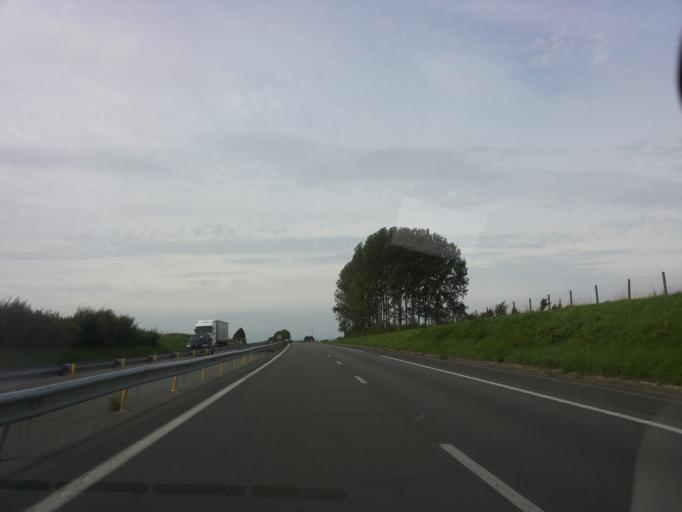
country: FR
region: Nord-Pas-de-Calais
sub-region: Departement du Pas-de-Calais
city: Burbure
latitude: 50.5583
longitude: 2.4348
